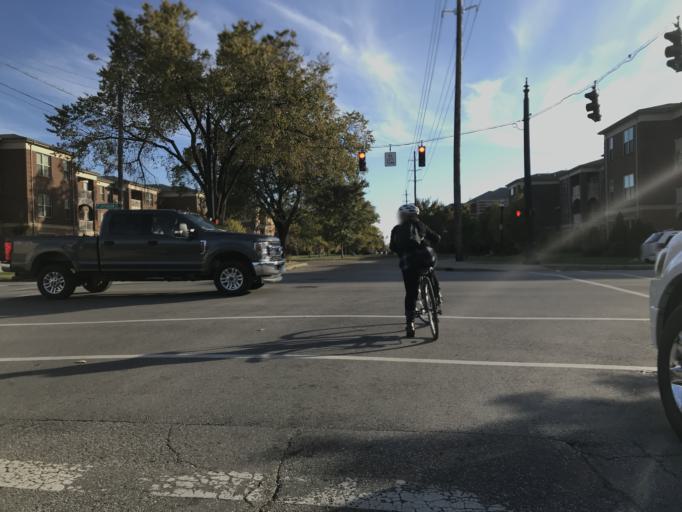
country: US
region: Kentucky
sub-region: Jefferson County
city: Louisville
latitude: 38.2523
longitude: -85.7403
